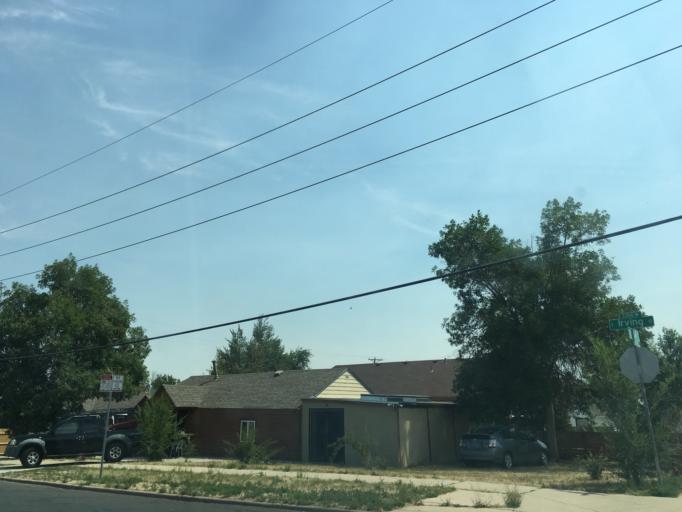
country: US
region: Colorado
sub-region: Jefferson County
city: Lakewood
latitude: 39.7049
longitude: -105.0298
